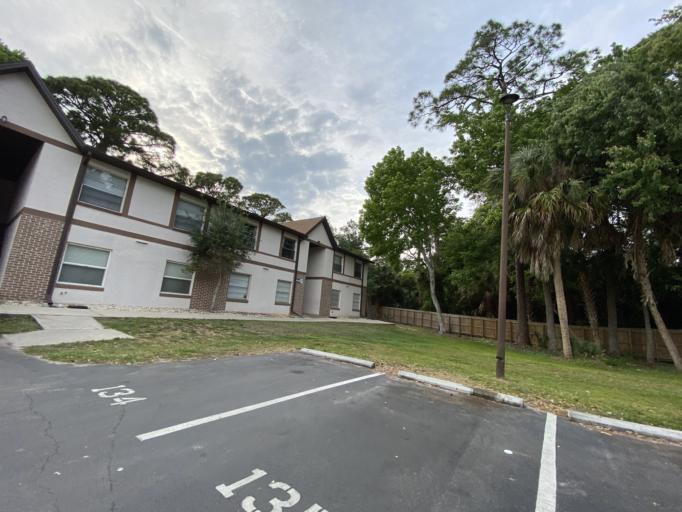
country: US
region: Florida
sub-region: Volusia County
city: South Daytona
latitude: 29.1610
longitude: -80.9989
